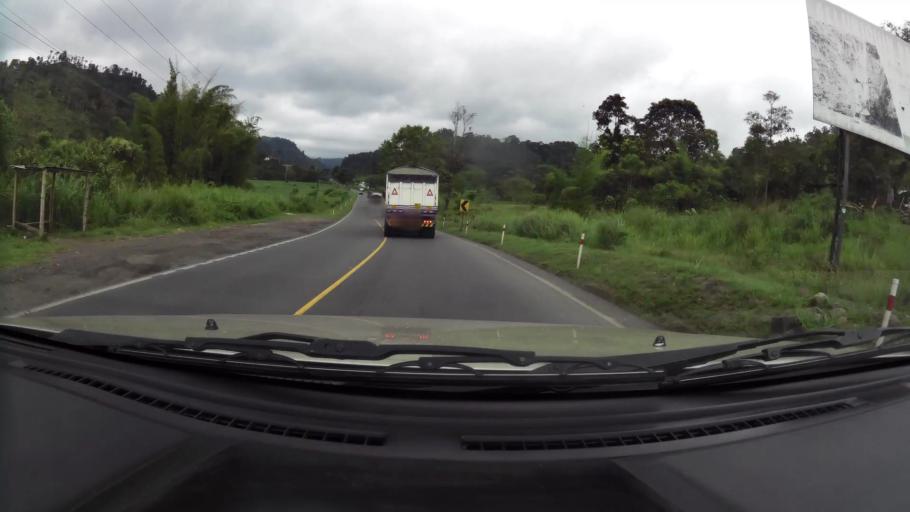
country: EC
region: Santo Domingo de los Tsachilas
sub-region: Canton Santo Domingo de los Colorados
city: Santo Domingo de los Colorados
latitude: -0.3104
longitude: -79.0382
